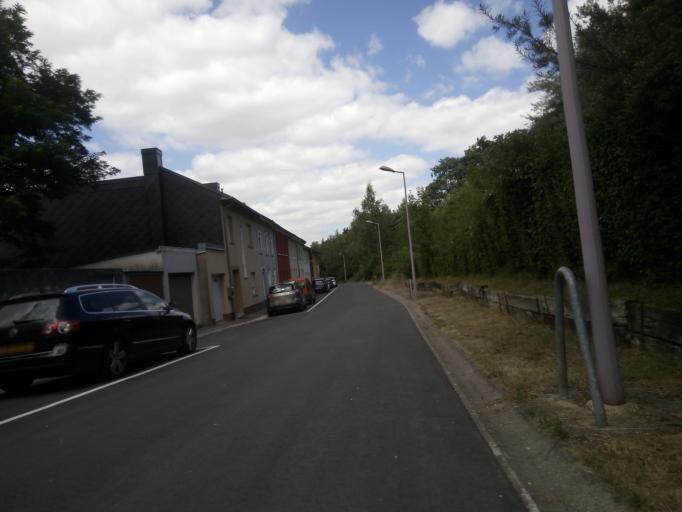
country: LU
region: Luxembourg
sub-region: Canton d'Esch-sur-Alzette
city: Petange
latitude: 49.5558
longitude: 5.8851
